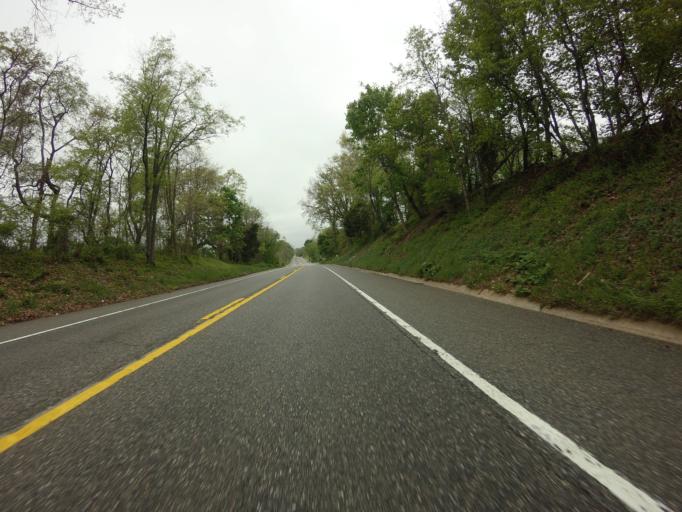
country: US
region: Maryland
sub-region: Washington County
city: Boonsboro
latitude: 39.5586
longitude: -77.6239
